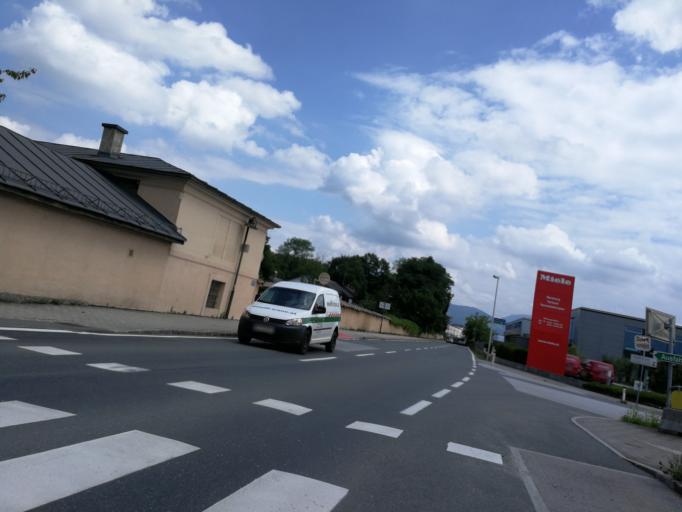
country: DE
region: Bavaria
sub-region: Upper Bavaria
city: Freilassing
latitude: 47.8159
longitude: 12.9905
